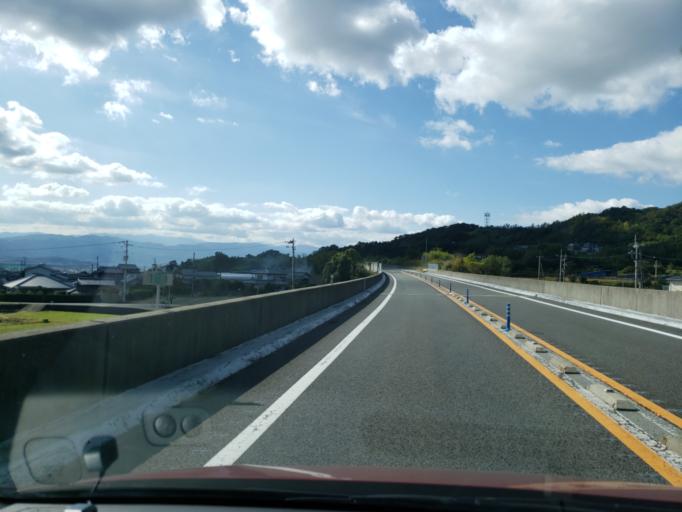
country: JP
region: Tokushima
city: Kamojimacho-jogejima
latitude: 34.1349
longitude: 134.3957
